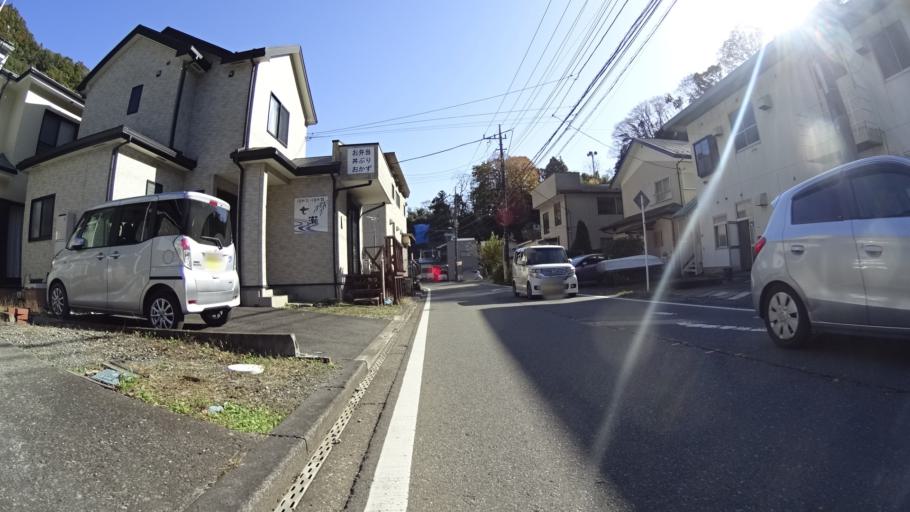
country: JP
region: Kanagawa
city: Zama
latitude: 35.5412
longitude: 139.2768
